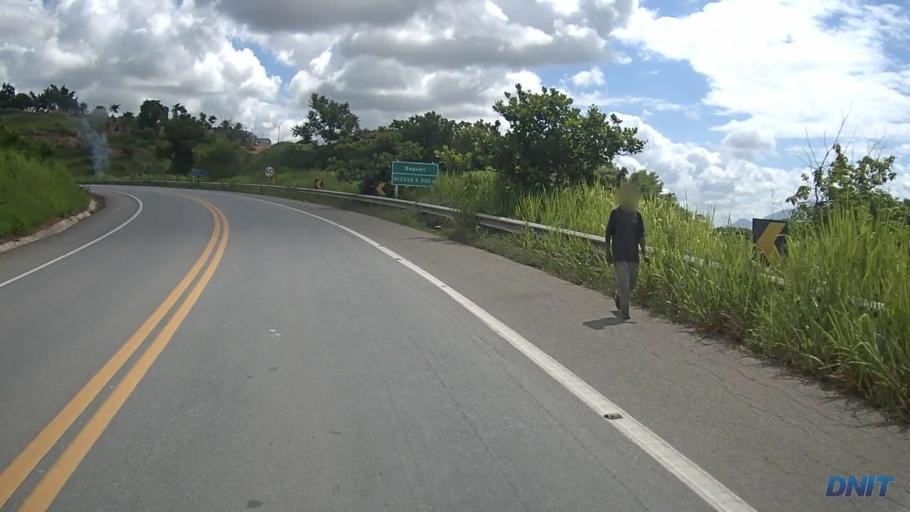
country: BR
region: Minas Gerais
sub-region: Governador Valadares
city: Governador Valadares
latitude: -18.9616
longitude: -42.0761
